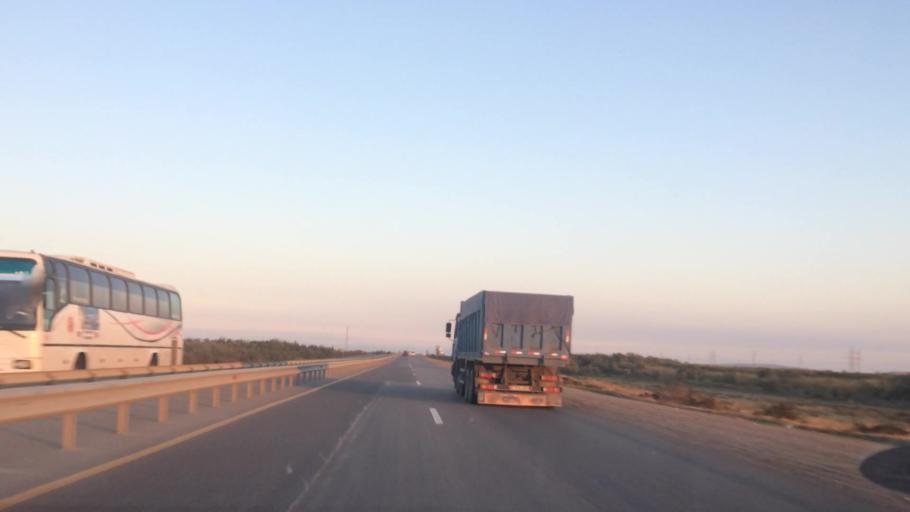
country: AZ
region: Baki
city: Qobustan
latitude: 39.9529
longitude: 49.3159
